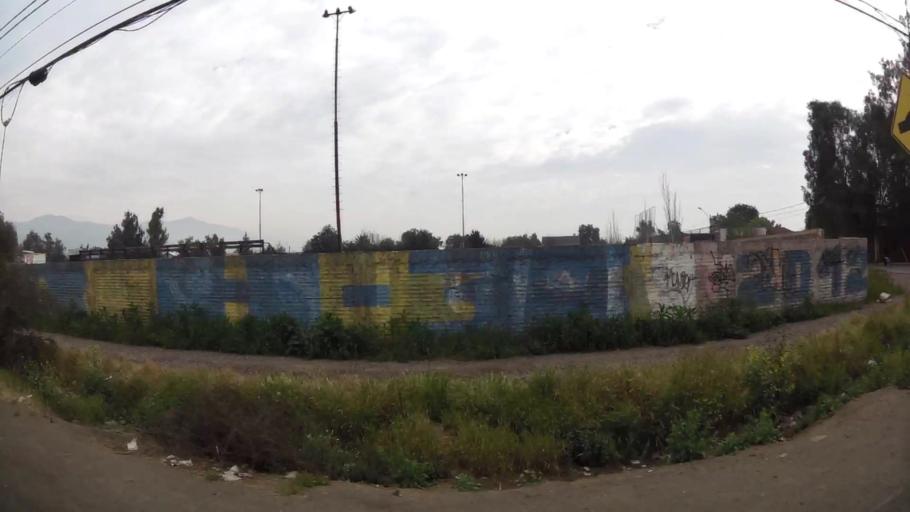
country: CL
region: Santiago Metropolitan
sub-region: Provincia de Chacabuco
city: Lampa
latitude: -33.2385
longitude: -70.8096
